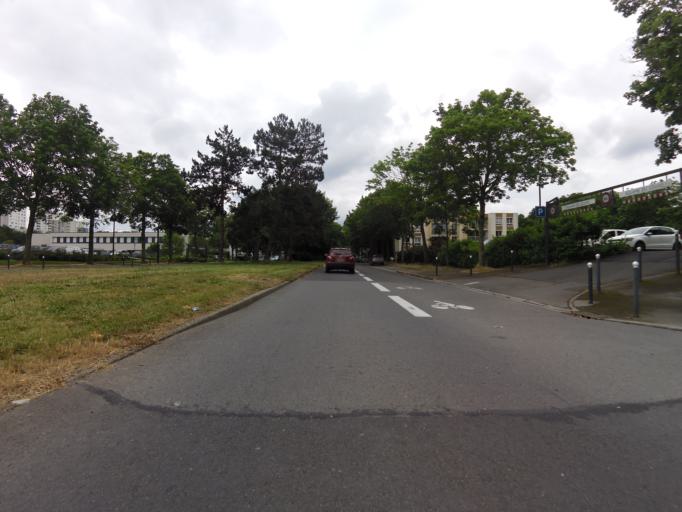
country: FR
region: Brittany
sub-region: Departement d'Ille-et-Vilaine
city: Rennes
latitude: 48.0835
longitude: -1.6678
